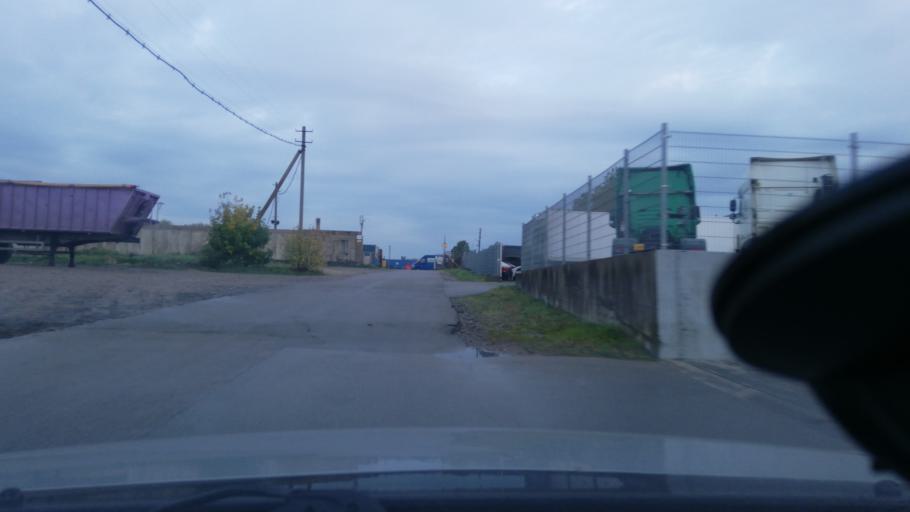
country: LT
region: Klaipedos apskritis
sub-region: Klaipeda
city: Klaipeda
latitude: 55.6868
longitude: 21.1855
